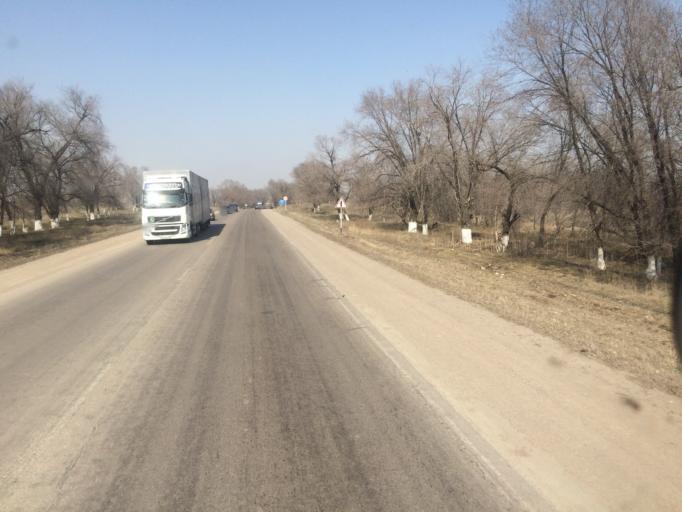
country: KZ
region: Almaty Oblysy
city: Burunday
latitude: 43.3243
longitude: 76.6629
